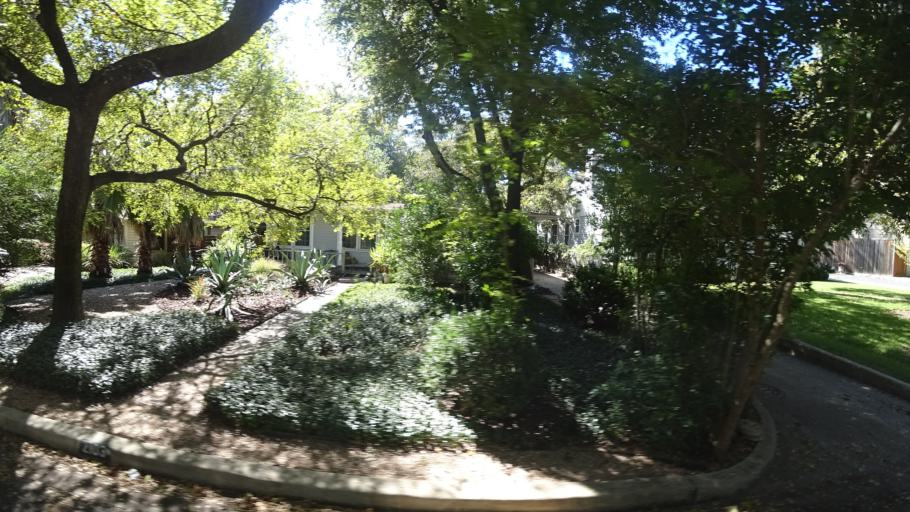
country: US
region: Texas
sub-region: Travis County
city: Austin
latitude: 30.2966
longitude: -97.7607
